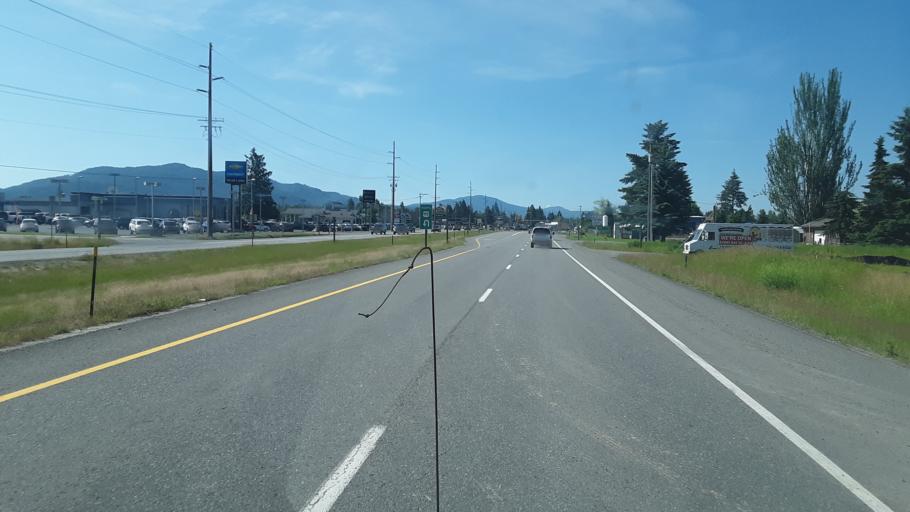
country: US
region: Idaho
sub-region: Bonner County
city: Ponderay
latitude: 48.3057
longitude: -116.5464
